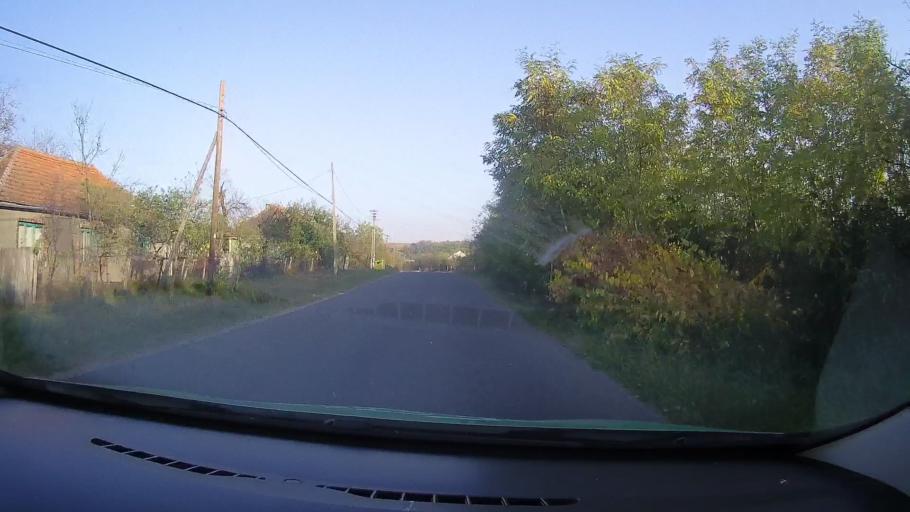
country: RO
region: Arad
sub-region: Comuna Silindia
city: Silindia
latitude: 46.3360
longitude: 21.9273
